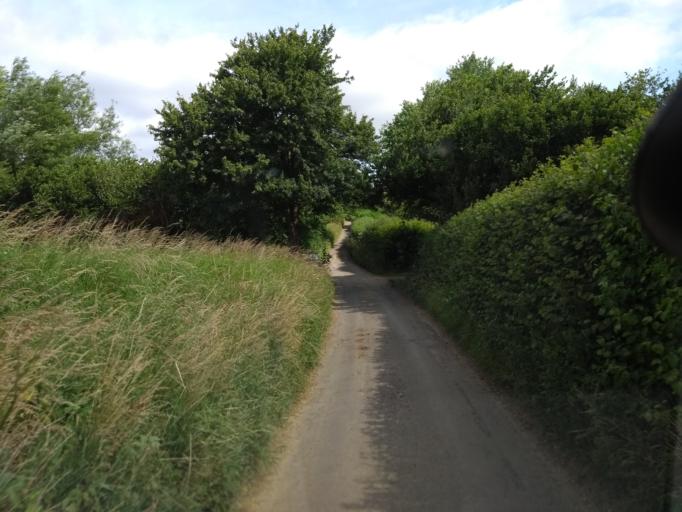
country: GB
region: England
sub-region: Somerset
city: Ilminster
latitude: 50.9217
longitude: -2.8650
